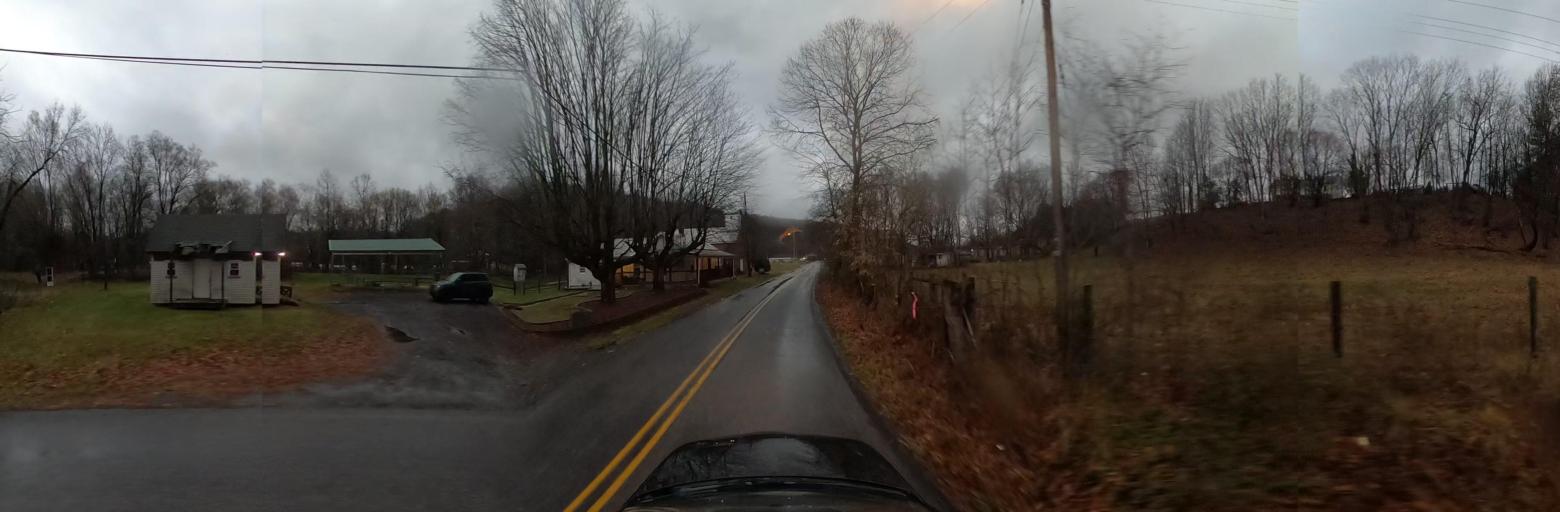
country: US
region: Virginia
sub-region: Augusta County
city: Jolivue
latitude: 38.1031
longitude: -79.3178
